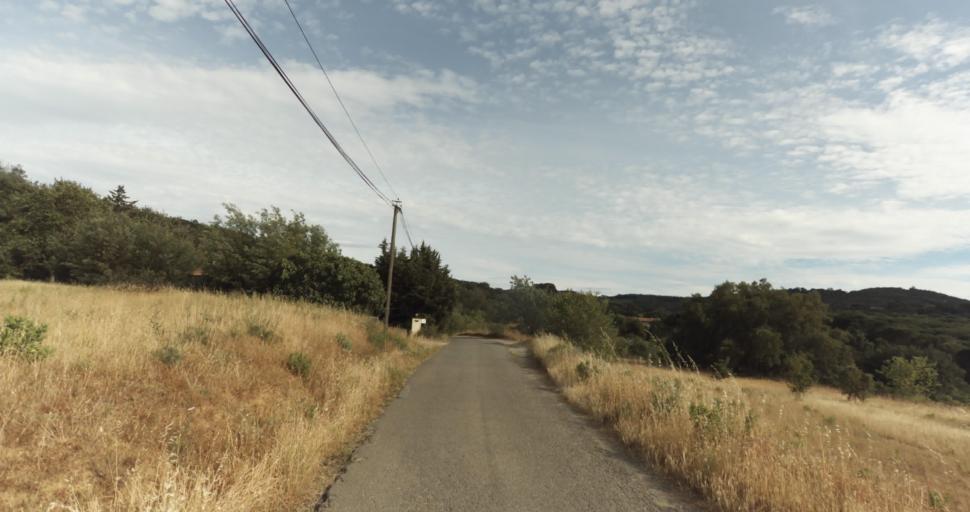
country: FR
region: Provence-Alpes-Cote d'Azur
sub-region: Departement du Var
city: Gassin
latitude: 43.2234
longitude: 6.5796
